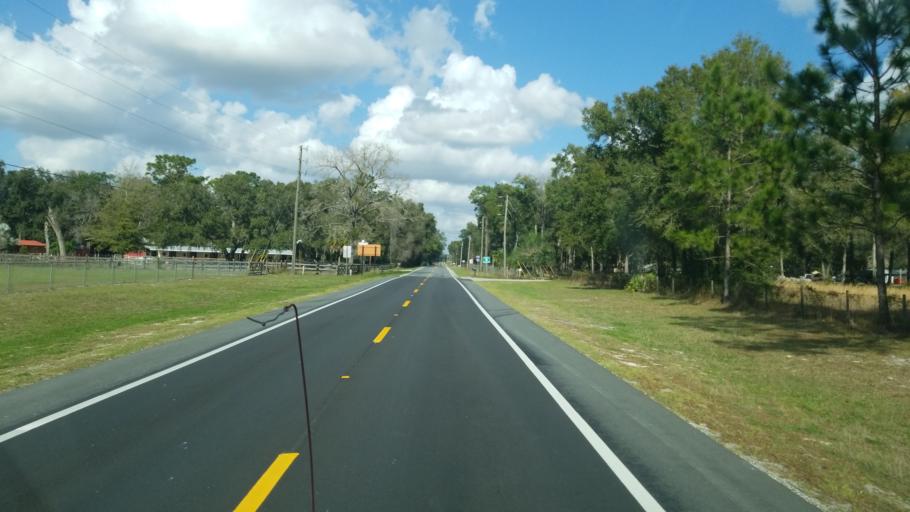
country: US
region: Florida
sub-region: Marion County
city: Belleview
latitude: 28.9593
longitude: -82.1199
